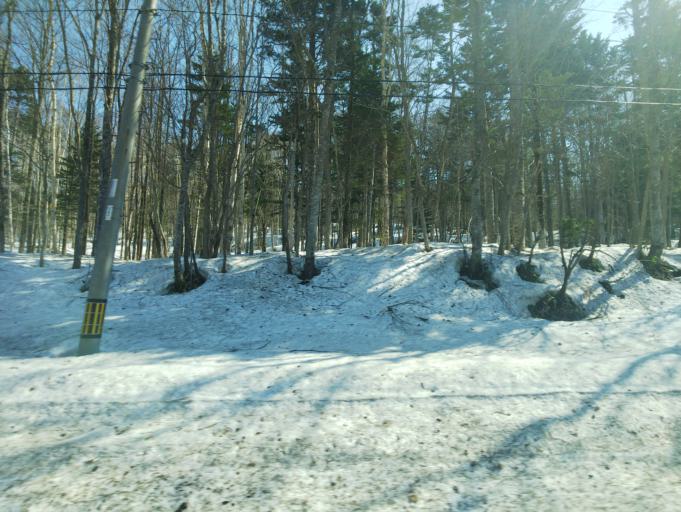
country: JP
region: Hokkaido
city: Nayoro
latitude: 44.7139
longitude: 142.2733
